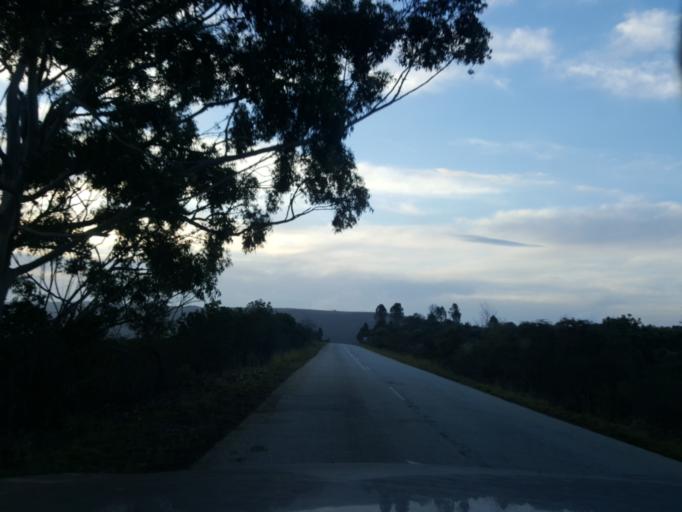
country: ZA
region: Eastern Cape
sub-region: Cacadu District Municipality
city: Grahamstown
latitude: -33.3849
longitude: 26.4715
